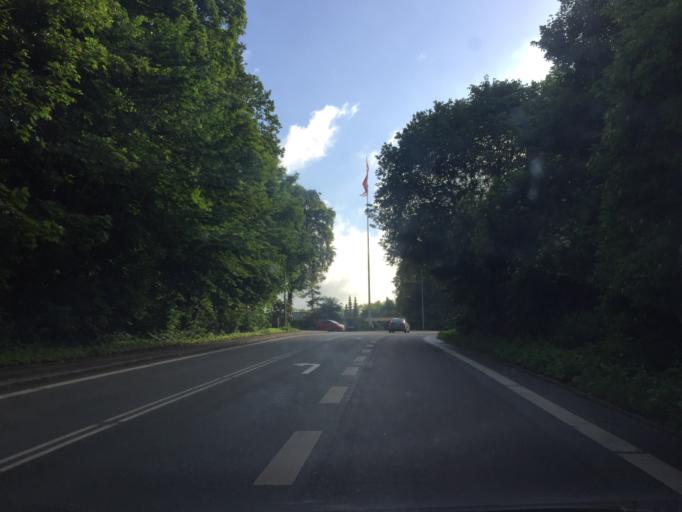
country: DK
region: Zealand
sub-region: Slagelse Kommune
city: Slagelse
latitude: 55.3917
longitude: 11.3627
